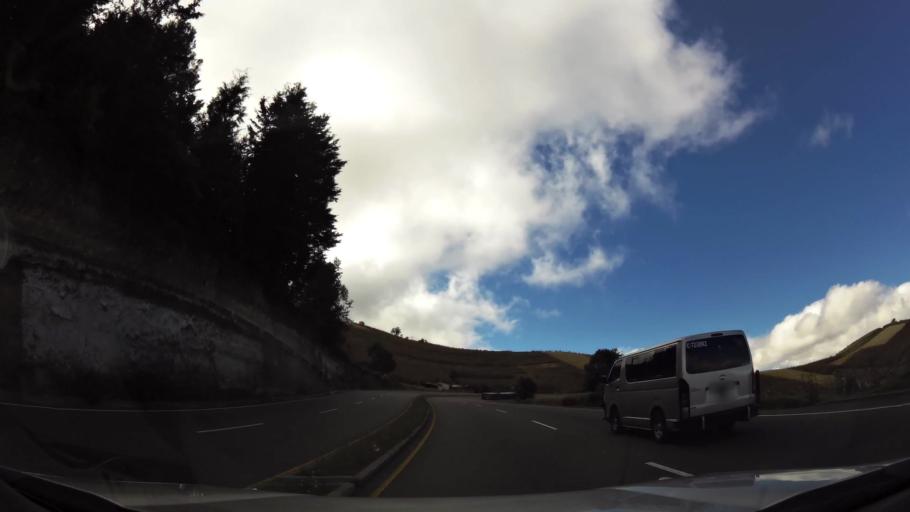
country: GT
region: Quetzaltenango
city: Salcaja
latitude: 14.8665
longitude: -91.4075
